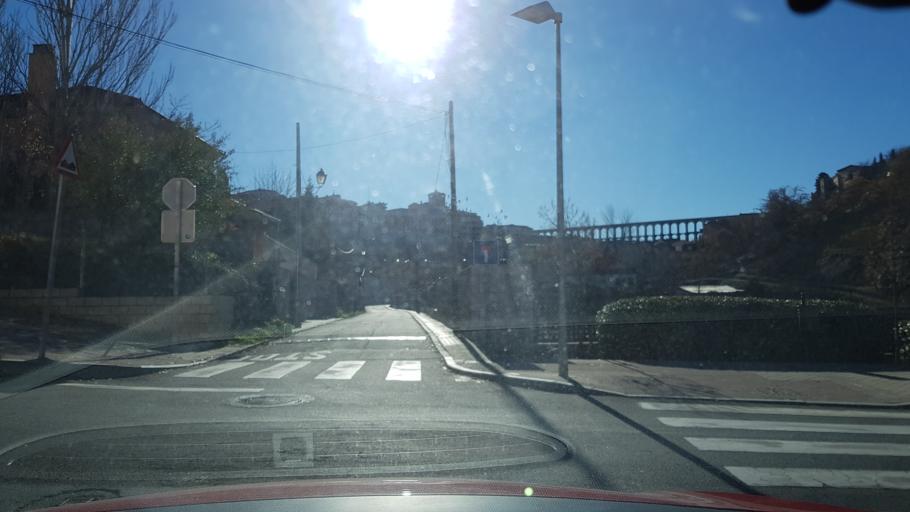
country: ES
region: Castille and Leon
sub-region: Provincia de Segovia
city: Segovia
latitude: 40.9514
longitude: -4.1134
